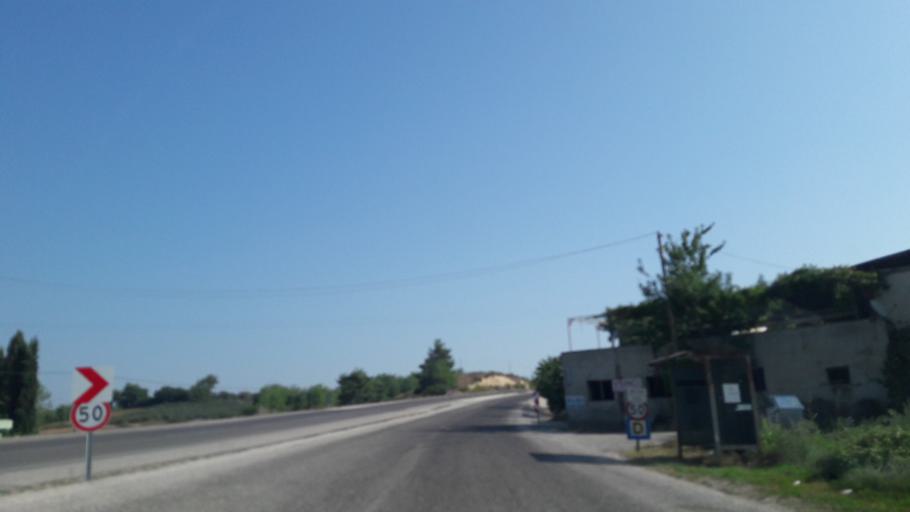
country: TR
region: Adana
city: Sagkaya
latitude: 37.1773
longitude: 35.5665
